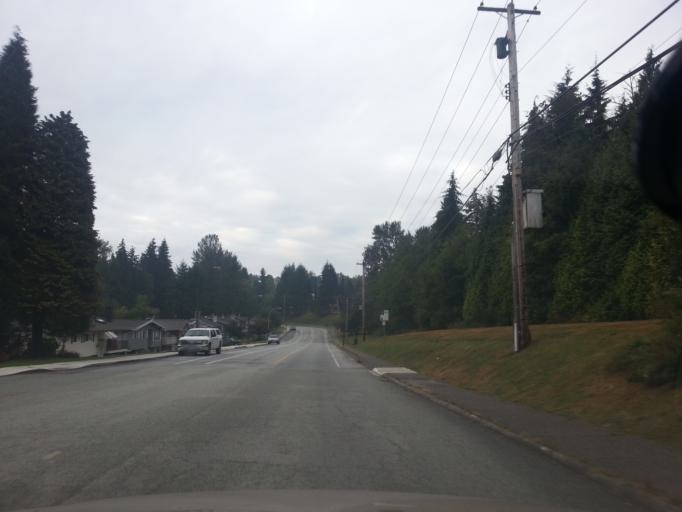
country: CA
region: British Columbia
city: Port Moody
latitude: 49.2818
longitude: -122.8799
